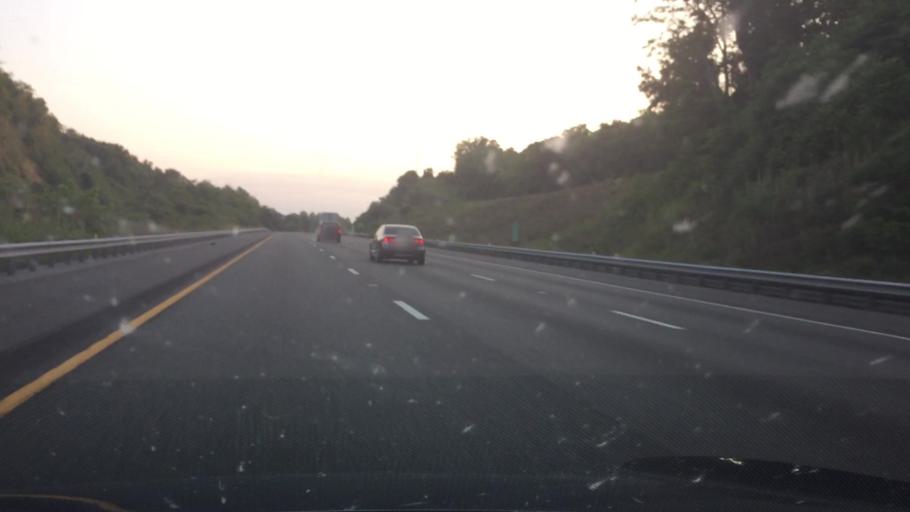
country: US
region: Virginia
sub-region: Montgomery County
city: Shawsville
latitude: 37.1888
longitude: -80.2807
